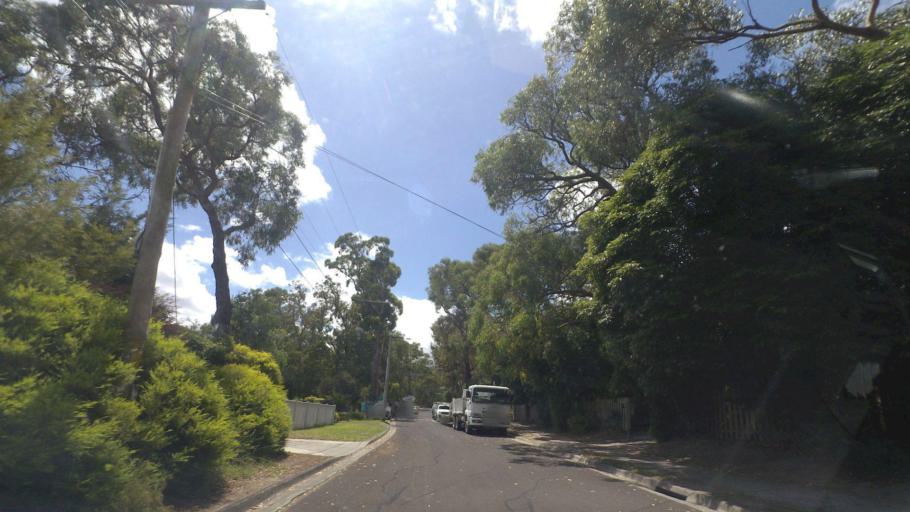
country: AU
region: Victoria
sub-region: Knox
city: Boronia
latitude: -37.8713
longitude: 145.2937
